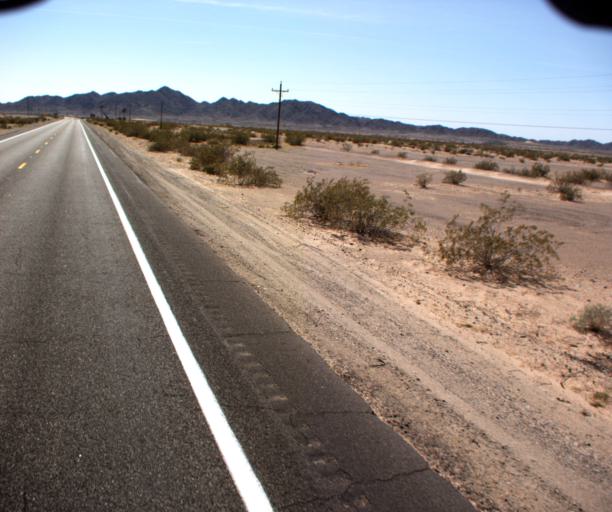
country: US
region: Arizona
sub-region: Yuma County
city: Fortuna Foothills
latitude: 32.8282
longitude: -114.3748
